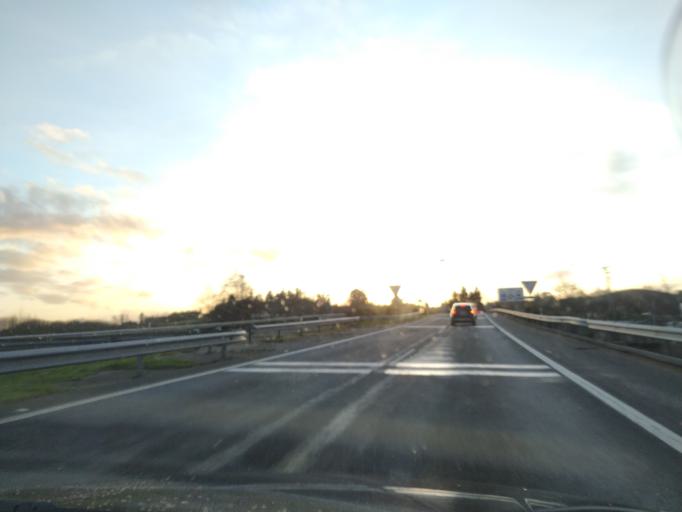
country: ES
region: Galicia
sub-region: Provincia da Coruna
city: Santiago de Compostela
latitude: 42.8995
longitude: -8.5069
